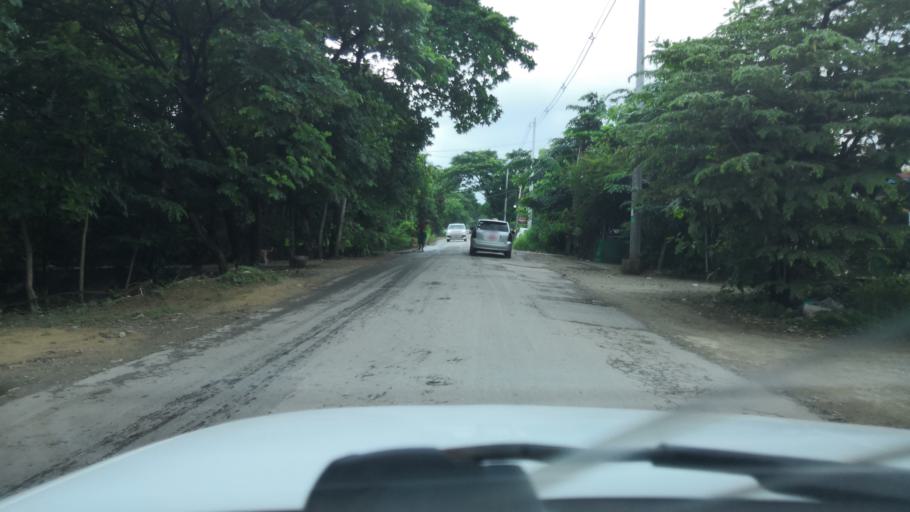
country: MM
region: Yangon
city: Yangon
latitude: 16.8812
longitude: 96.1794
